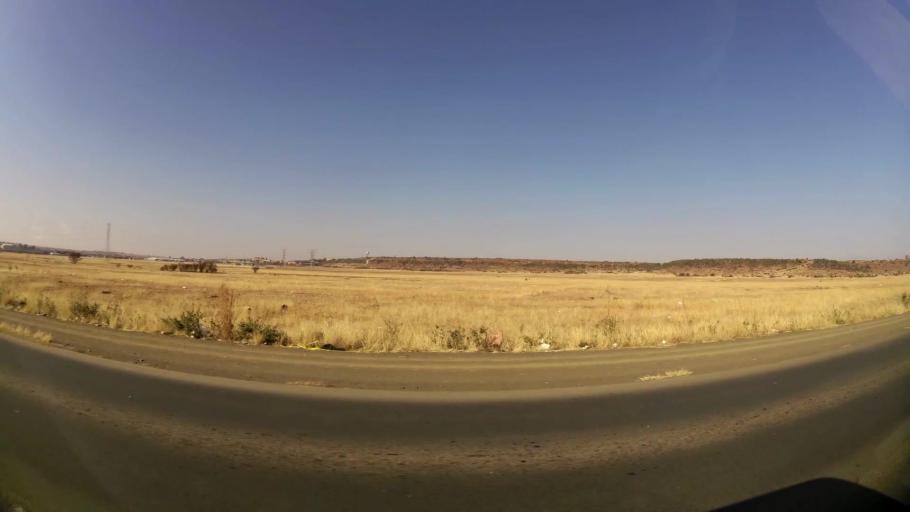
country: ZA
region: Orange Free State
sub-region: Mangaung Metropolitan Municipality
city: Bloemfontein
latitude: -29.1721
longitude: 26.2100
